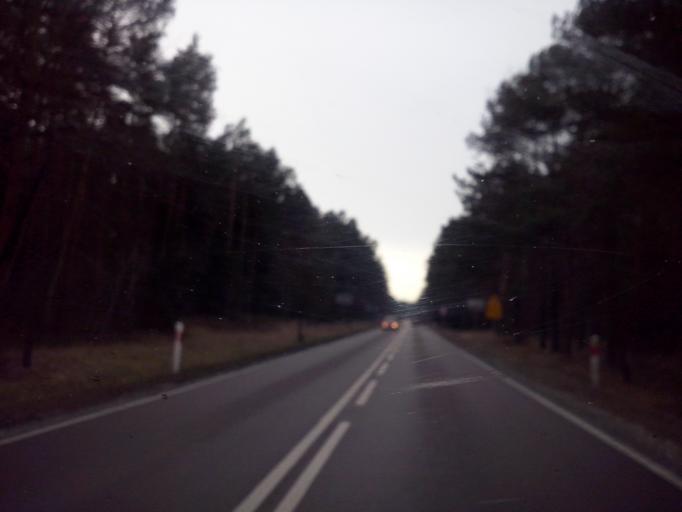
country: PL
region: Lublin Voivodeship
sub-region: Powiat bilgorajski
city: Tereszpol
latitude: 50.5812
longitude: 22.7985
